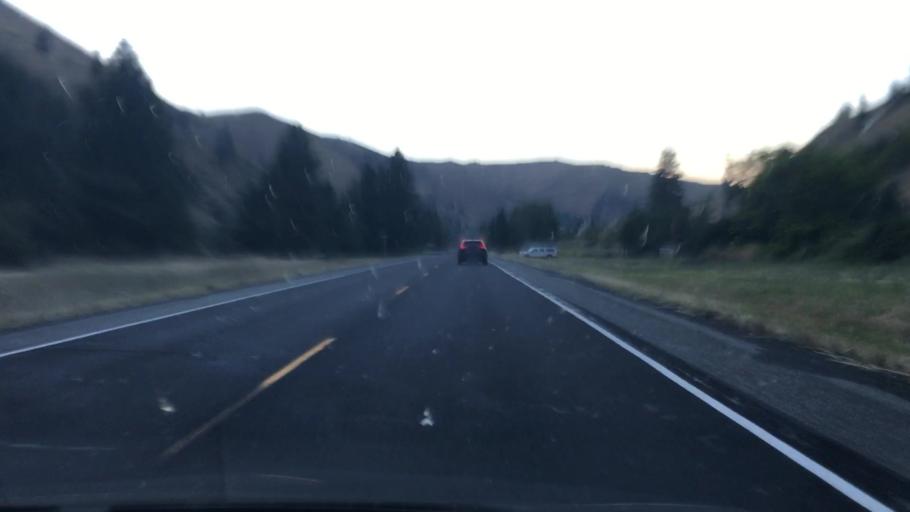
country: US
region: Idaho
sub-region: Valley County
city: McCall
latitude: 45.2923
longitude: -116.3571
